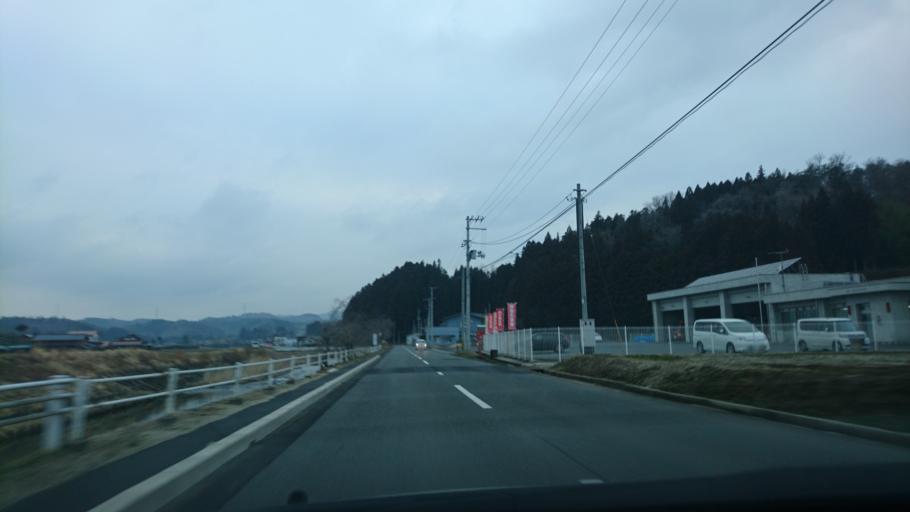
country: JP
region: Iwate
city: Ichinoseki
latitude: 39.0196
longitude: 141.3375
